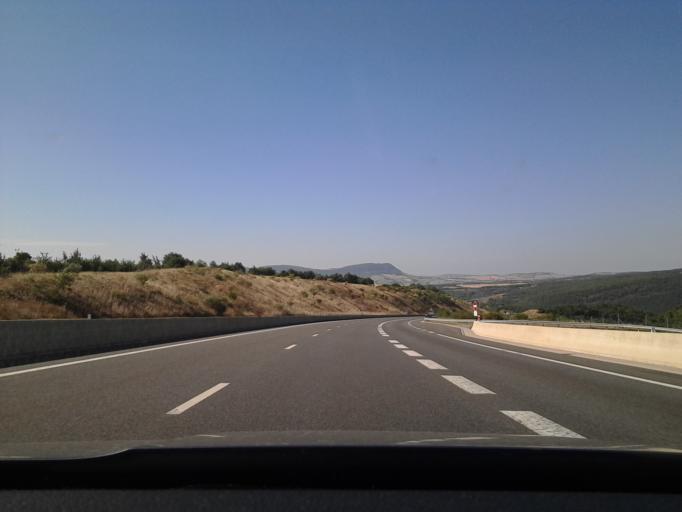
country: FR
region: Midi-Pyrenees
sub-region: Departement de l'Aveyron
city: Severac-le-Chateau
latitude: 44.2181
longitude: 3.0724
